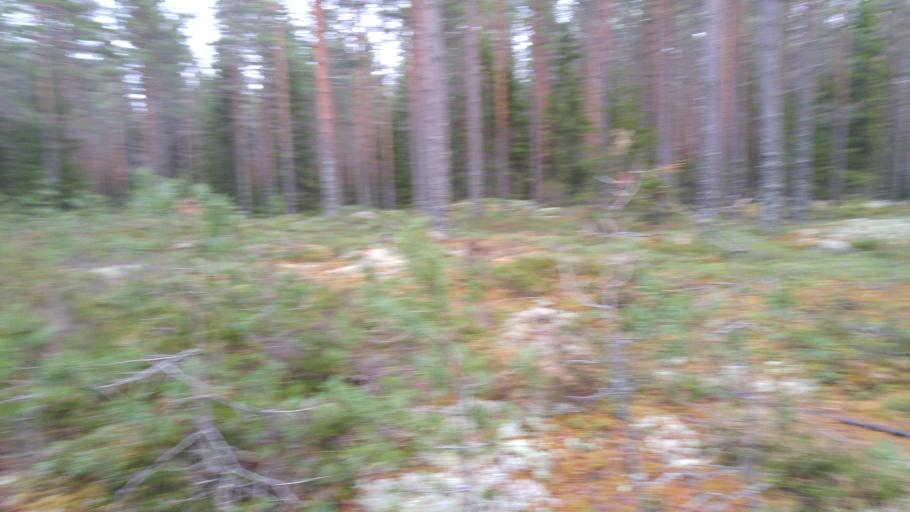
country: FI
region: Pirkanmaa
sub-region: Tampere
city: Kangasala
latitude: 61.6028
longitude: 23.9786
